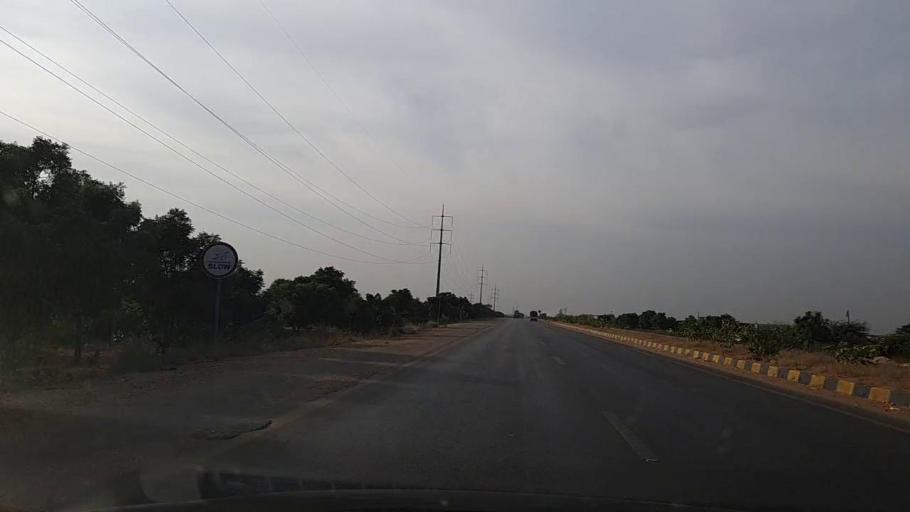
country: PK
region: Sindh
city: Gharo
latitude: 24.8333
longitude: 67.4593
